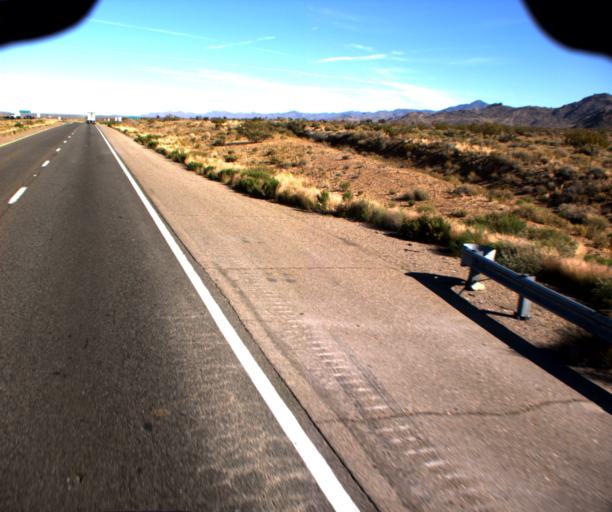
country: US
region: Arizona
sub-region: Mohave County
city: Golden Valley
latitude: 35.2488
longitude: -114.1519
